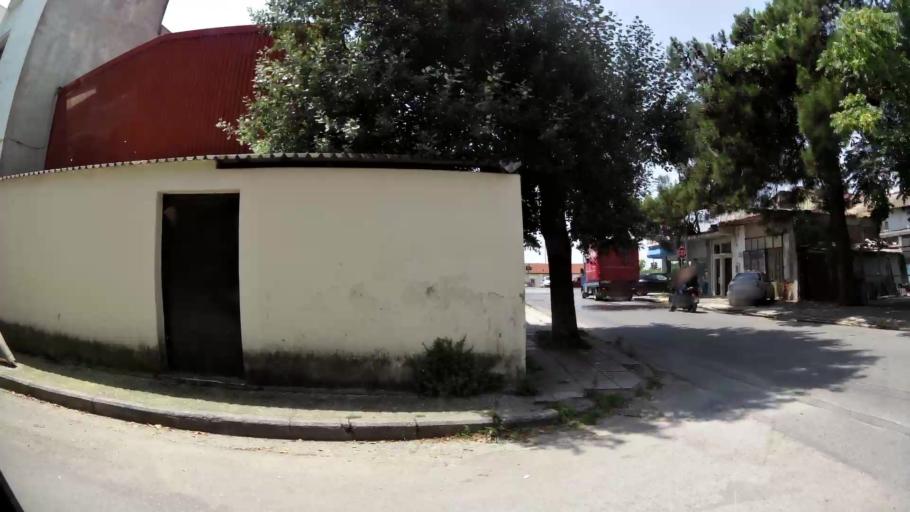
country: GR
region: Central Macedonia
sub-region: Nomos Thessalonikis
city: Menemeni
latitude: 40.6692
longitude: 22.8881
